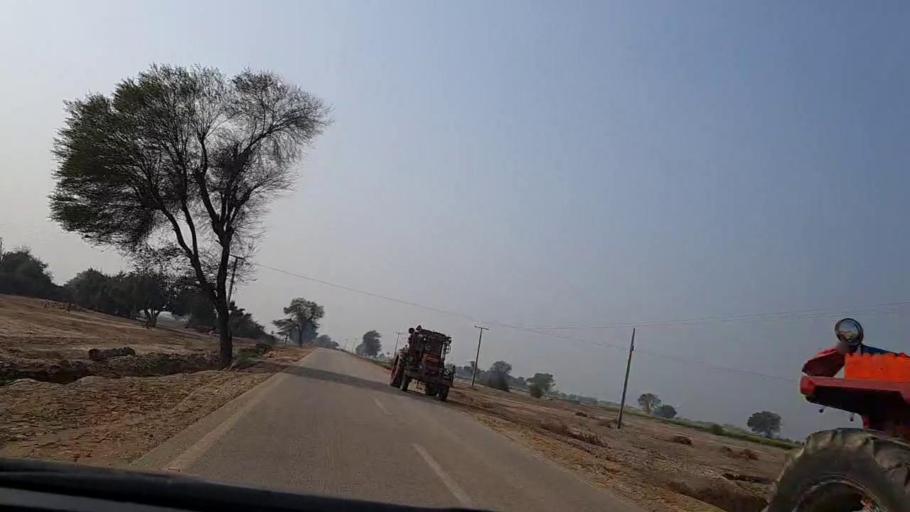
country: PK
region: Sindh
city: Sakrand
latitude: 26.1350
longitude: 68.1933
